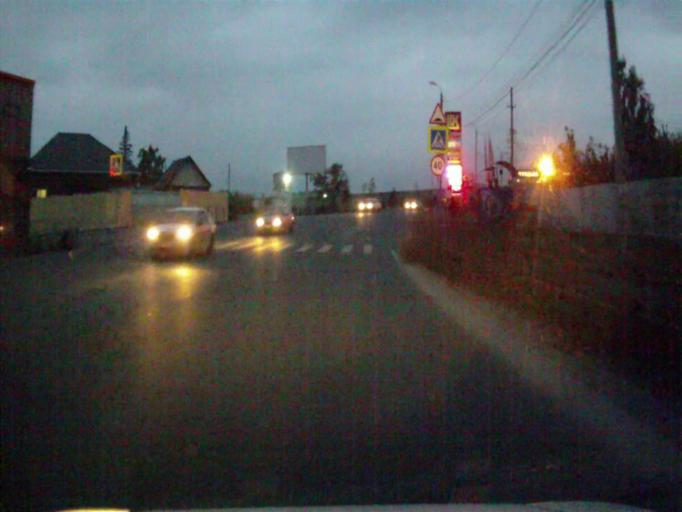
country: RU
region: Chelyabinsk
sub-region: Gorod Chelyabinsk
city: Chelyabinsk
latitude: 55.1529
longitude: 61.3035
